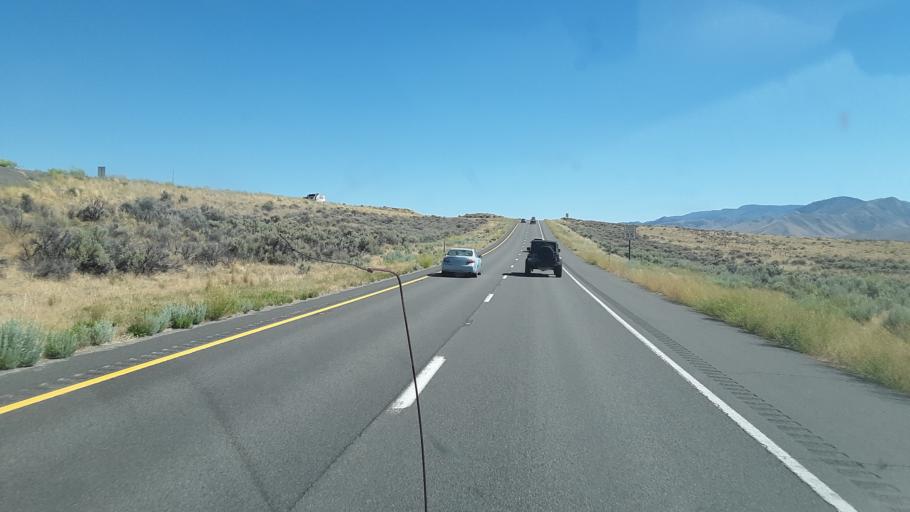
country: US
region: Nevada
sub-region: Washoe County
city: Cold Springs
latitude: 39.7654
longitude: -120.0391
